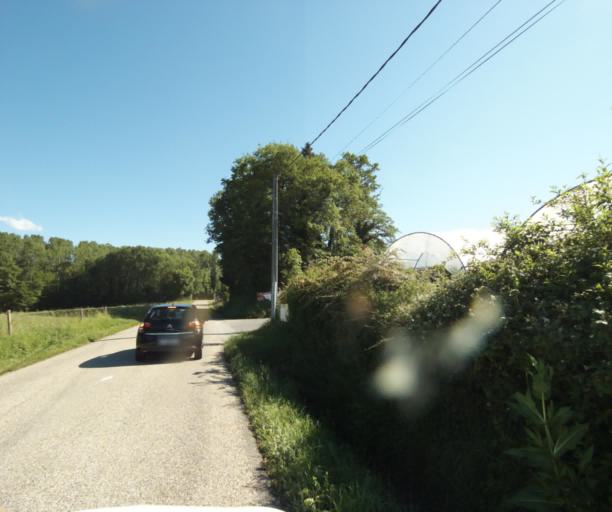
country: FR
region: Rhone-Alpes
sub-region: Departement de la Haute-Savoie
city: Sciez
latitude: 46.3104
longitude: 6.3821
